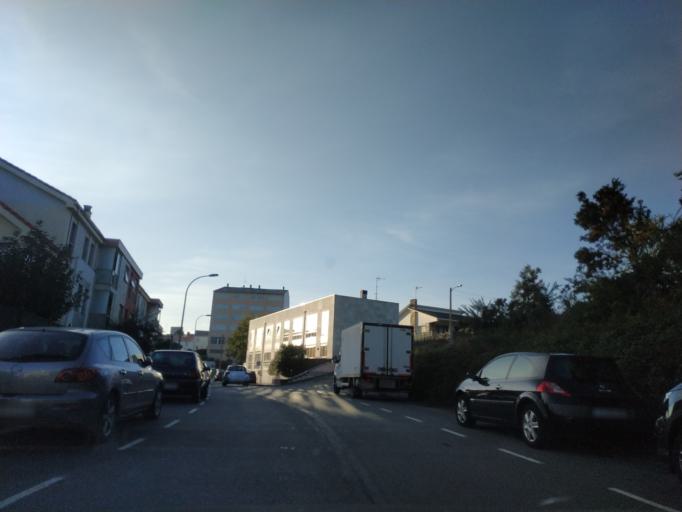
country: ES
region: Galicia
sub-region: Provincia da Coruna
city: Oleiros
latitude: 43.3507
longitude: -8.3438
